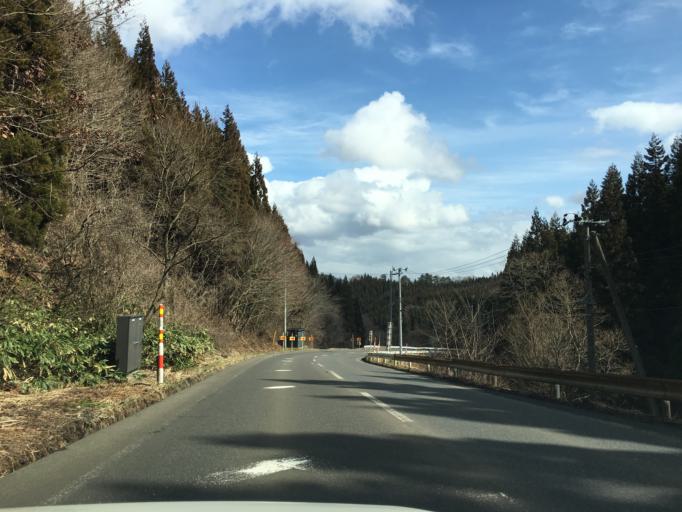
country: JP
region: Akita
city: Odate
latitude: 40.1925
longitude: 140.5230
